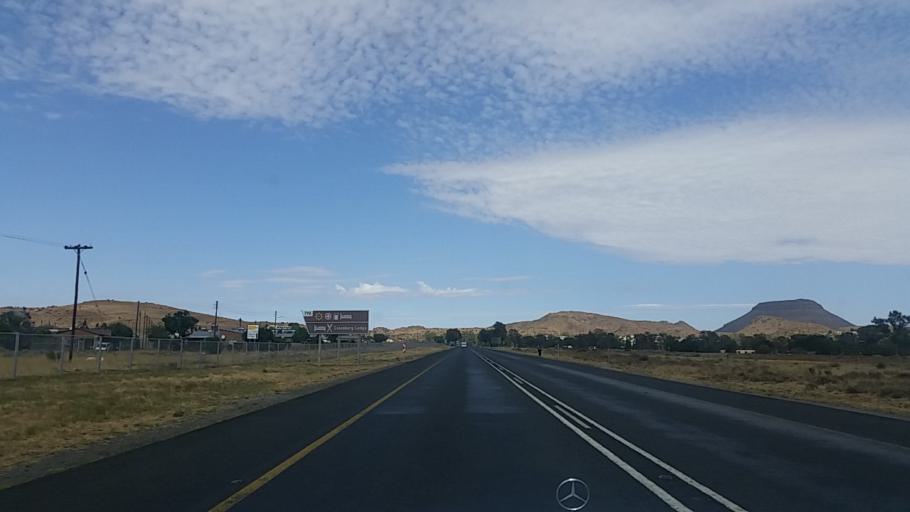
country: ZA
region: Northern Cape
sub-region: Pixley ka Seme District Municipality
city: Colesberg
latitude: -30.7055
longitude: 25.1146
